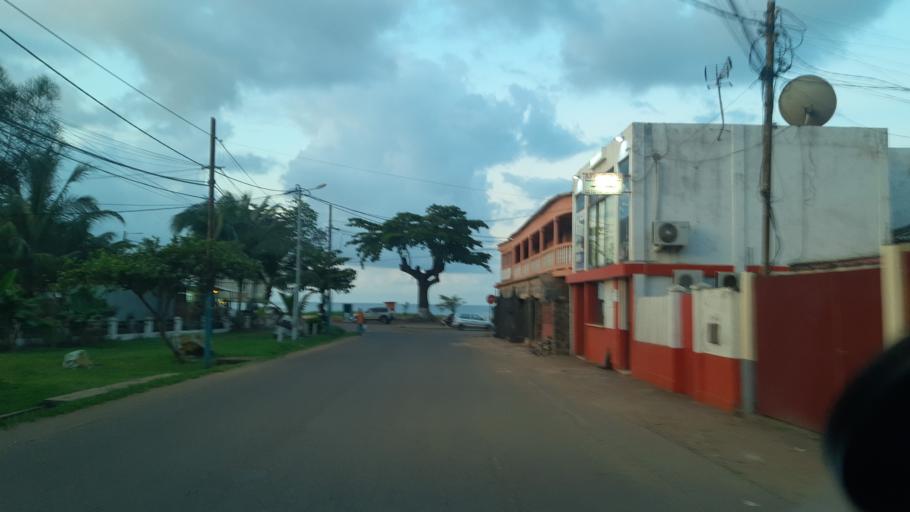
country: ST
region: Sao Tome Island
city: Sao Tome
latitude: 0.3340
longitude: 6.7388
